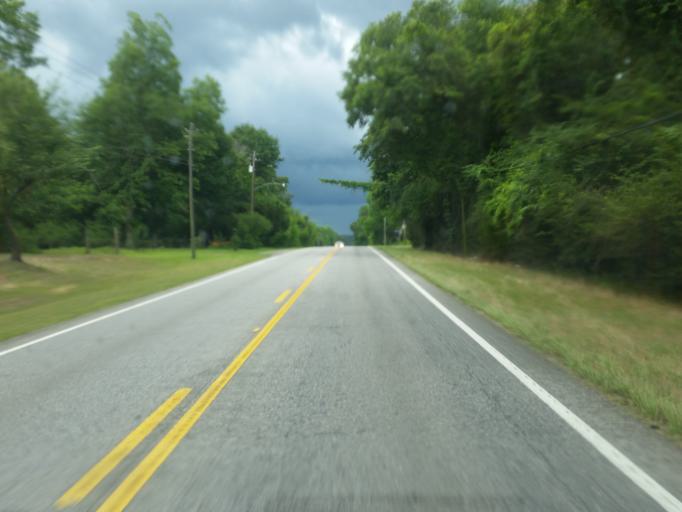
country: US
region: Mississippi
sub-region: Jackson County
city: Hurley
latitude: 30.8108
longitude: -88.3423
